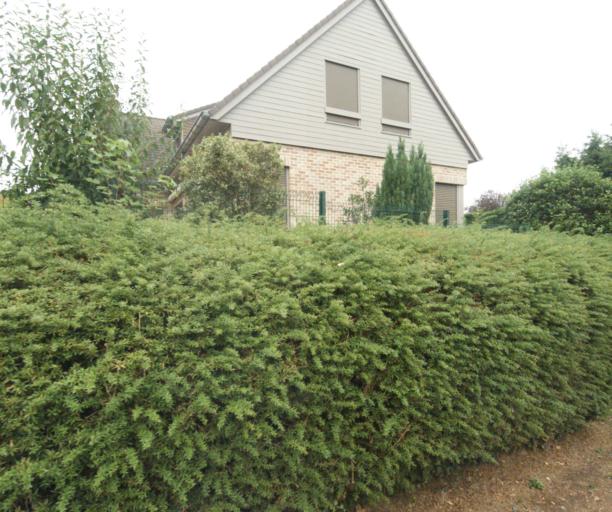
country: FR
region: Nord-Pas-de-Calais
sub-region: Departement du Nord
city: Mons-en-Baroeul
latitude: 50.6454
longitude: 3.1089
